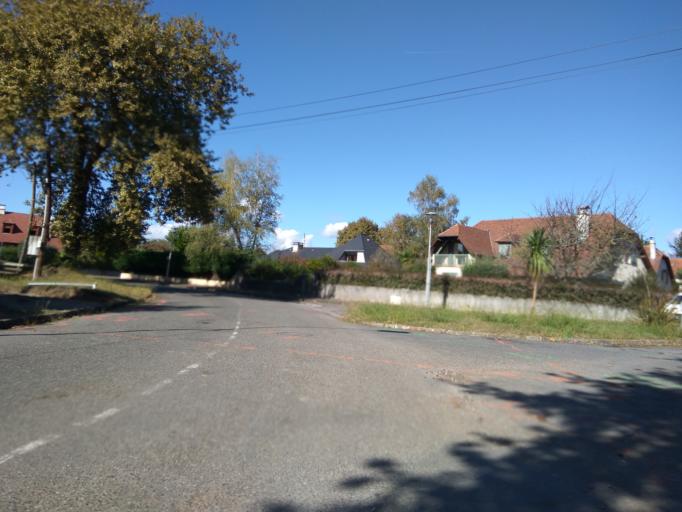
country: FR
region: Aquitaine
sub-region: Departement des Pyrenees-Atlantiques
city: Idron
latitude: 43.2996
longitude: -0.3139
